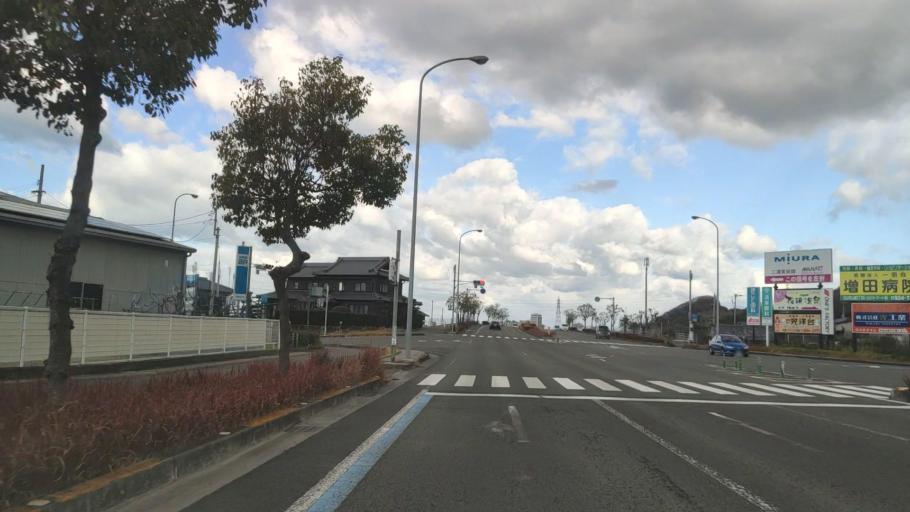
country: JP
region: Ehime
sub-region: Shikoku-chuo Shi
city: Matsuyama
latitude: 33.8985
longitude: 132.7578
